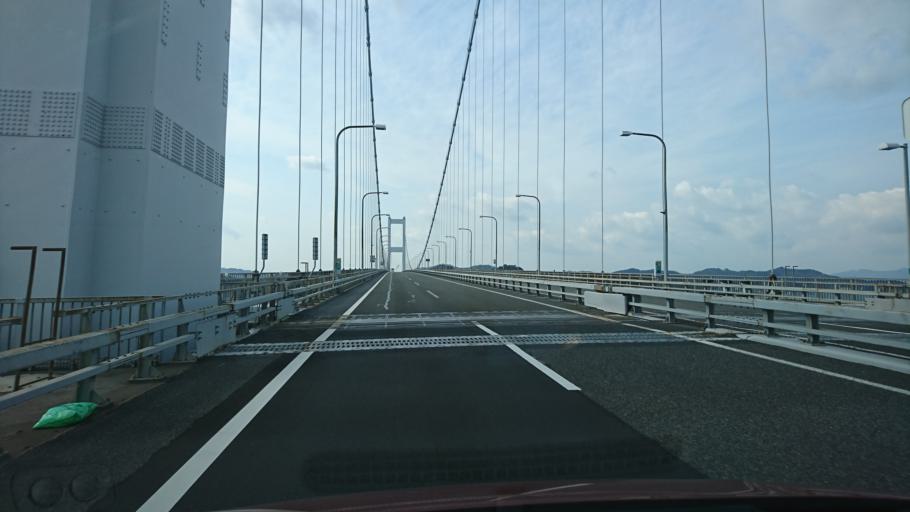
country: JP
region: Hiroshima
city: Takehara
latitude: 34.1172
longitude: 132.9898
